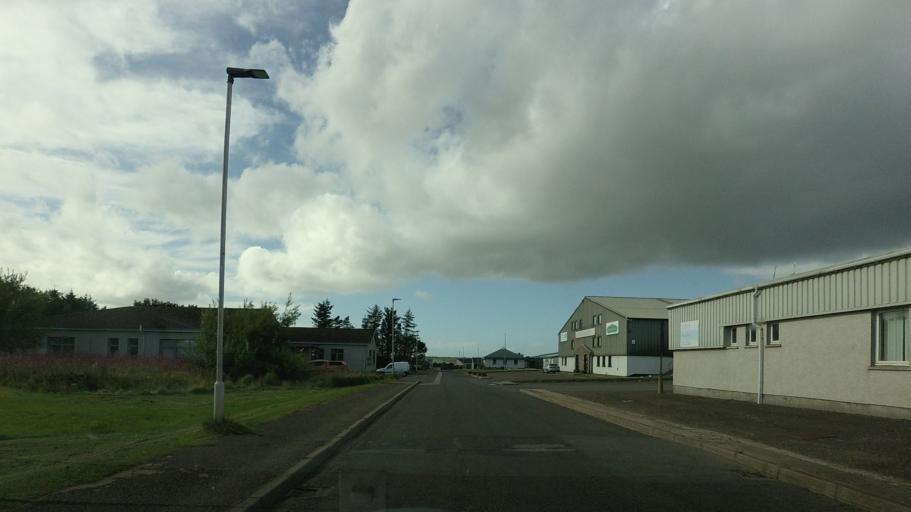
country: GB
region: Scotland
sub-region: Highland
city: Wick
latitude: 58.4495
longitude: -3.0908
